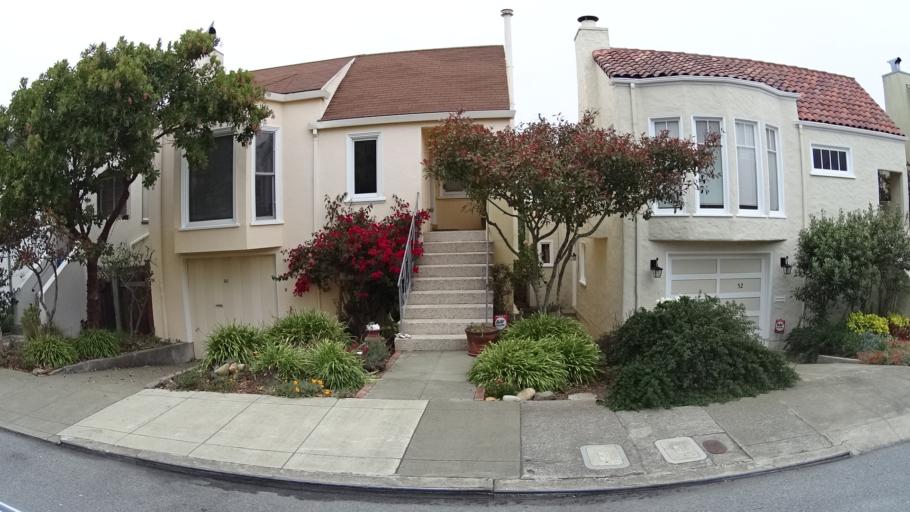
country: US
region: California
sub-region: San Mateo County
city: Daly City
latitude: 37.7422
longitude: -122.4522
